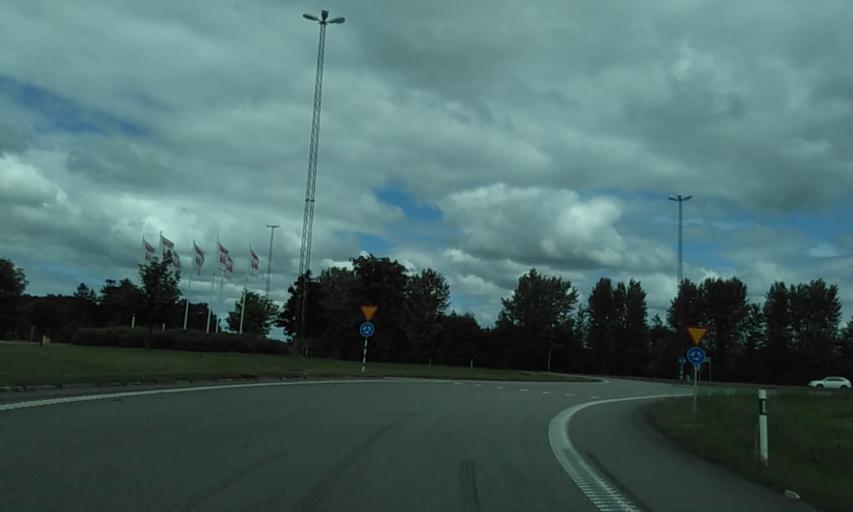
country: SE
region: Vaestra Goetaland
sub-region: Skara Kommun
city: Skara
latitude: 58.3812
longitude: 13.4100
